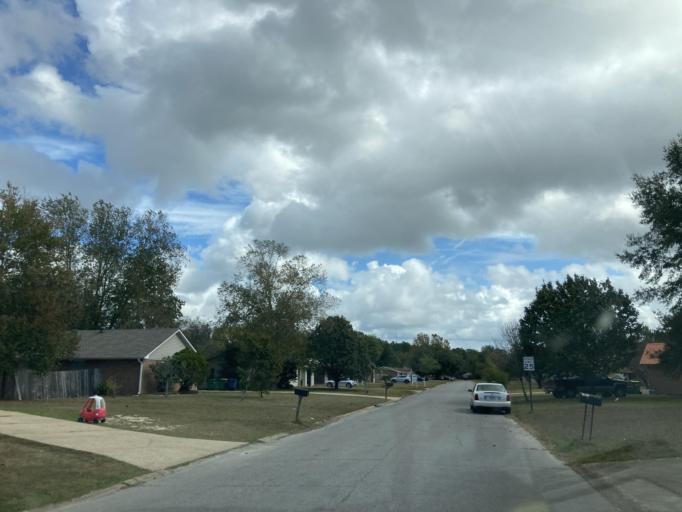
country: US
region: Mississippi
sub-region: Jackson County
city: Gulf Hills
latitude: 30.4462
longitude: -88.8302
